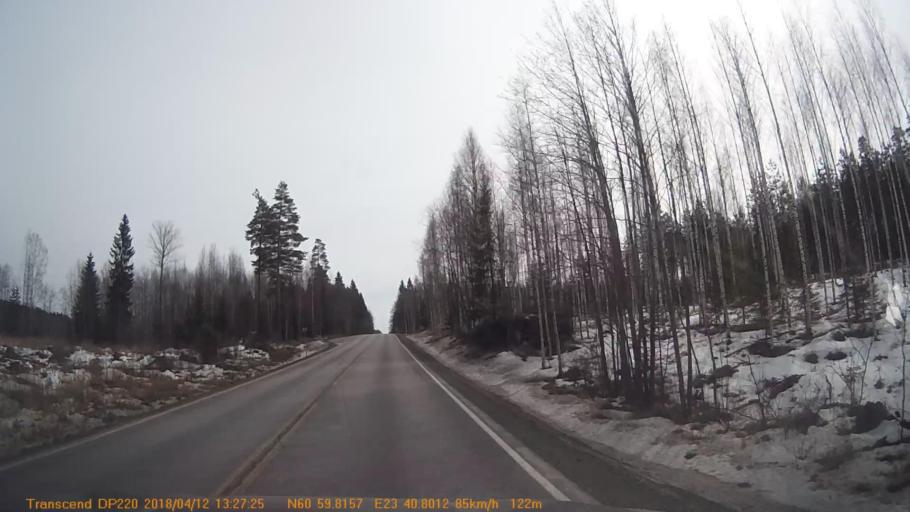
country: FI
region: Pirkanmaa
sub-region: Etelae-Pirkanmaa
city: Kylmaekoski
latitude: 60.9968
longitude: 23.6802
